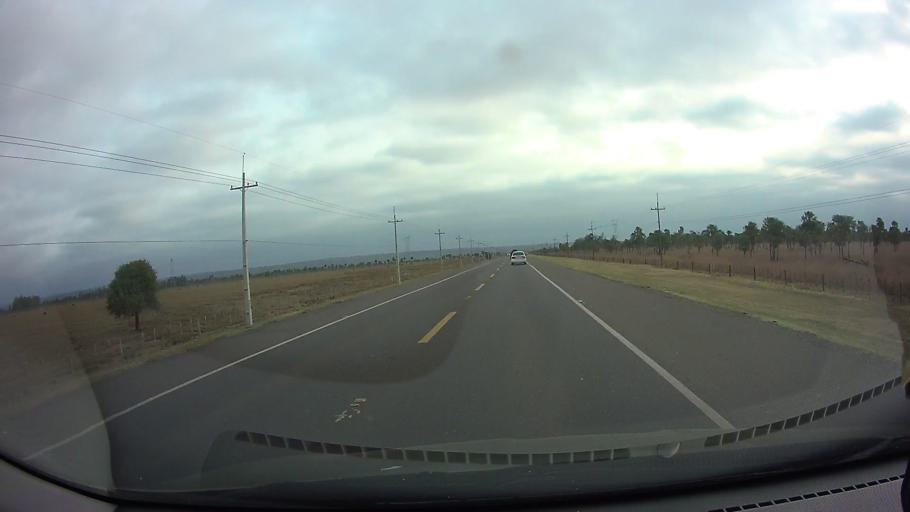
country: PY
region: Cordillera
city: Emboscada
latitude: -25.0794
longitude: -57.2728
